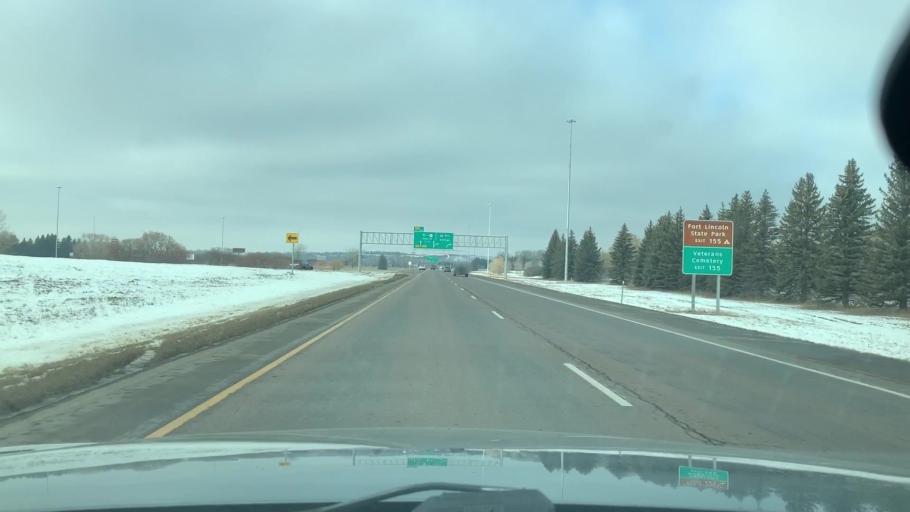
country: US
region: North Dakota
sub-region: Morton County
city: Mandan
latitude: 46.8225
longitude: -100.8421
